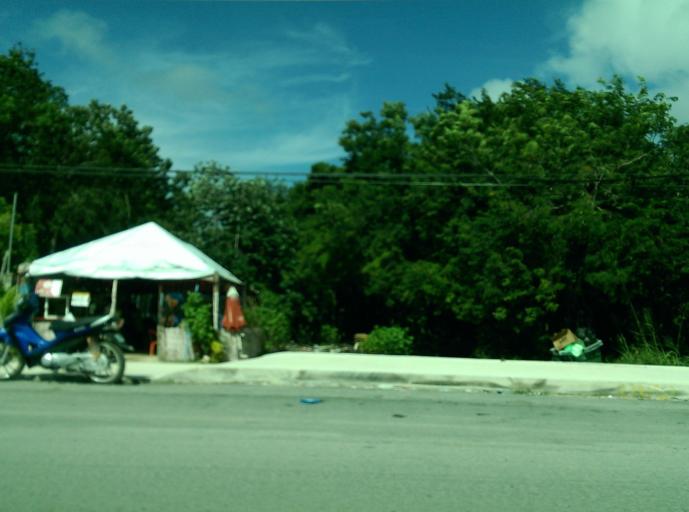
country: MX
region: Quintana Roo
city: Tulum
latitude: 20.2132
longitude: -87.4565
